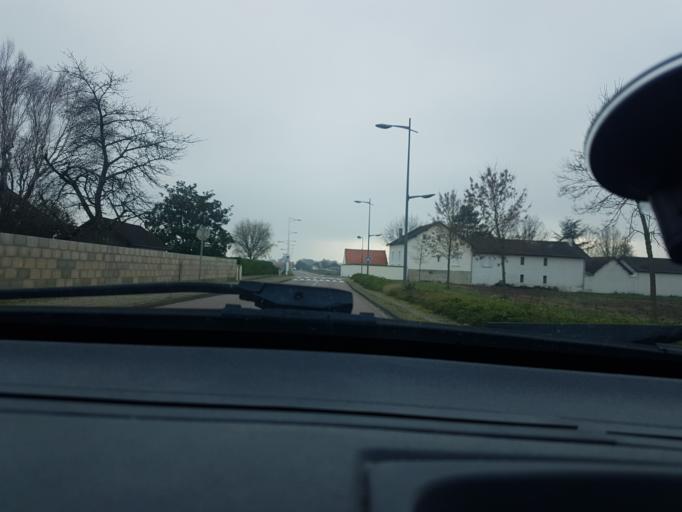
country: FR
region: Bourgogne
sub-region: Departement de Saone-et-Loire
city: Chatenoy-le-Royal
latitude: 46.7856
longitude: 4.8070
